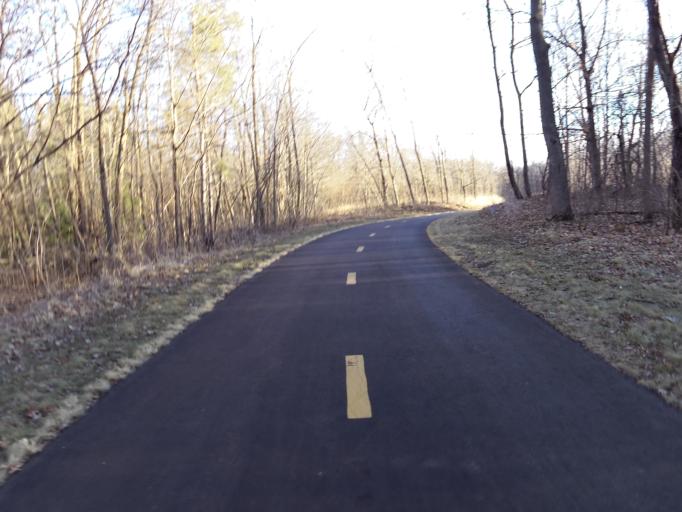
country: US
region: Minnesota
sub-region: Scott County
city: Prior Lake
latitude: 44.7229
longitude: -93.4674
